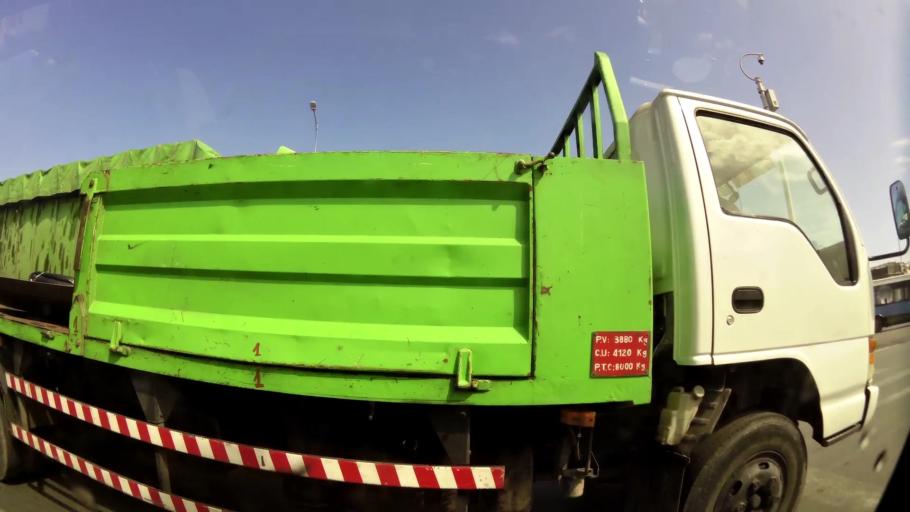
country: MA
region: Grand Casablanca
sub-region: Mediouna
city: Tit Mellil
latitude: 33.6196
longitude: -7.5340
